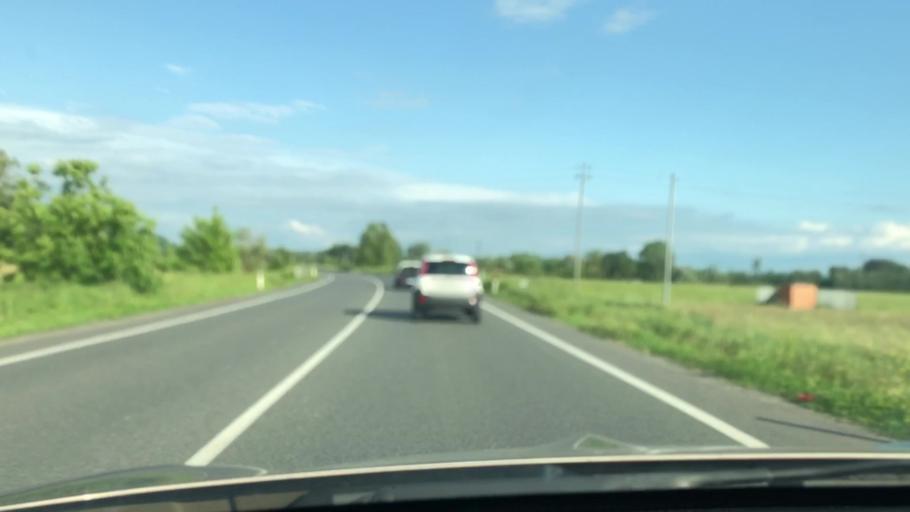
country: IT
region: Tuscany
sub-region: Province of Pisa
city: Treggiaia
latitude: 43.6202
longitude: 10.6665
